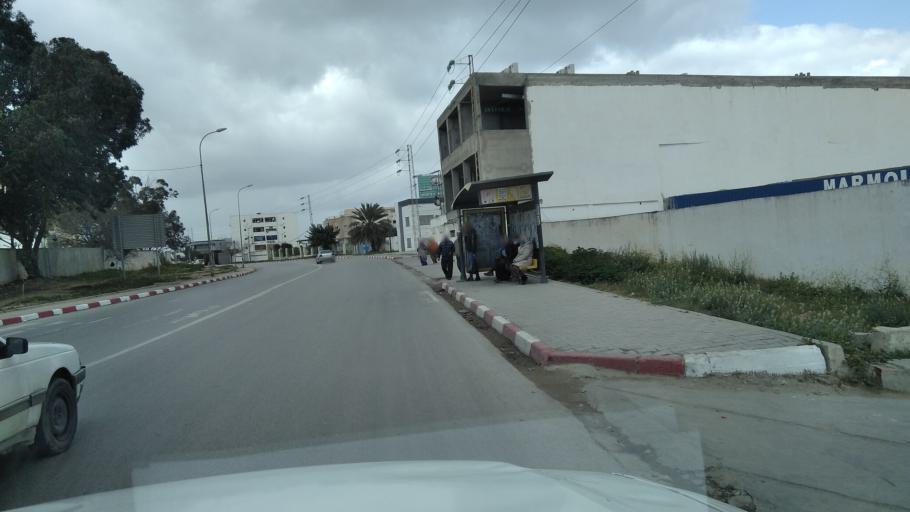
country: TN
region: Bin 'Arus
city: Ben Arous
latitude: 36.7452
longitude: 10.2335
